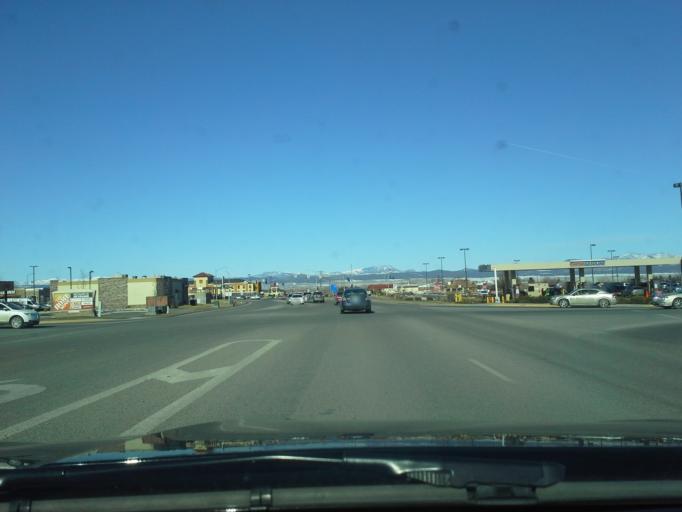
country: US
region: Montana
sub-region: Lewis and Clark County
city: Helena
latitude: 46.6142
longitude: -112.0048
